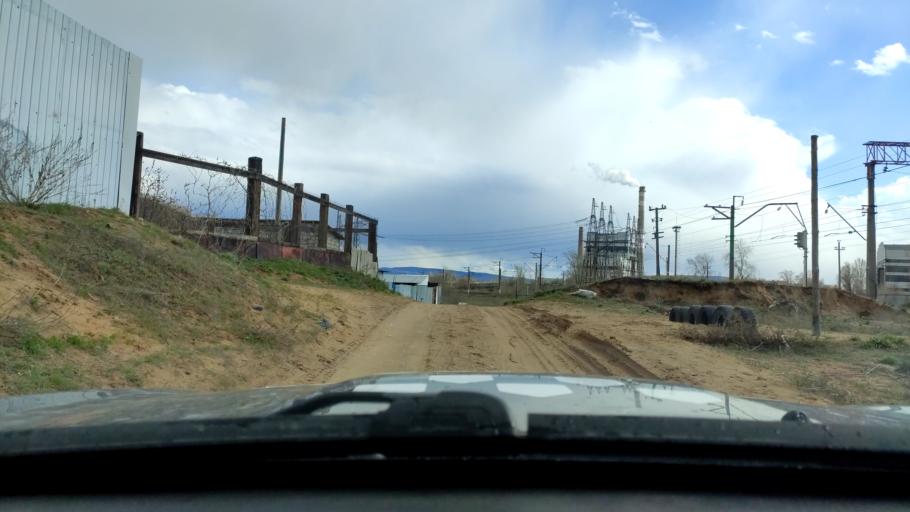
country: RU
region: Samara
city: Zhigulevsk
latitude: 53.4939
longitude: 49.4914
